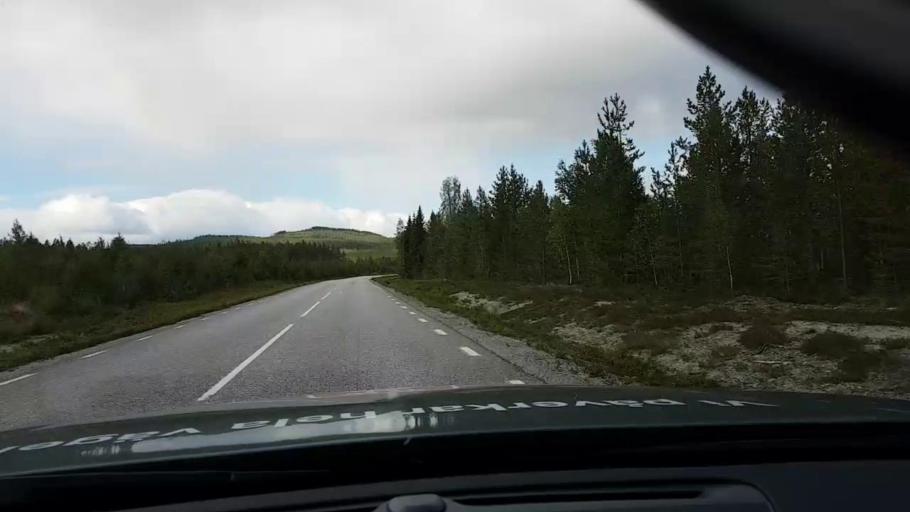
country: SE
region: Vaesternorrland
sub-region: OErnskoeldsviks Kommun
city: Bredbyn
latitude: 63.6792
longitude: 17.7883
